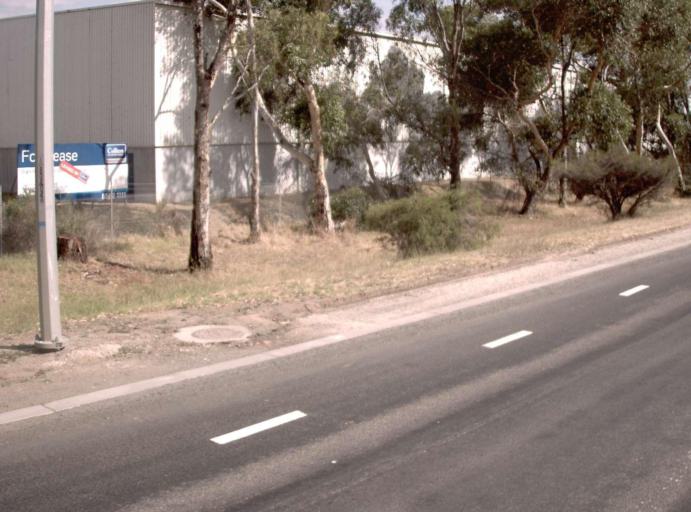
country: AU
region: Victoria
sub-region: Casey
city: Hampton Park
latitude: -38.0213
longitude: 145.2478
